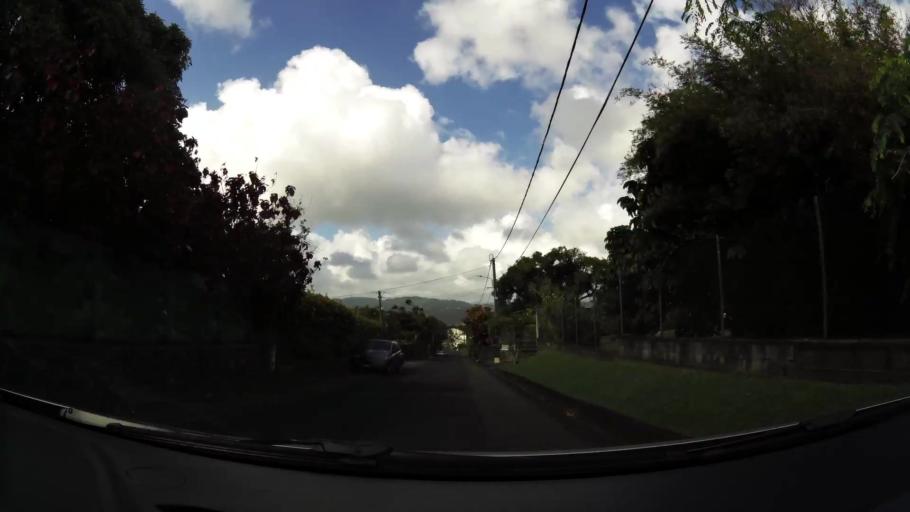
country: MQ
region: Martinique
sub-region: Martinique
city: Saint-Joseph
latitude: 14.6422
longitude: -61.0548
